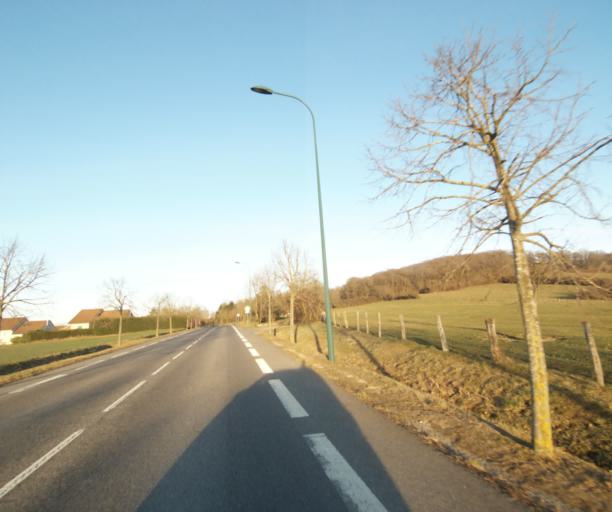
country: FR
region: Lorraine
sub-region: Departement de Meurthe-et-Moselle
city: Saulxures-les-Nancy
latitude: 48.6940
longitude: 6.2538
